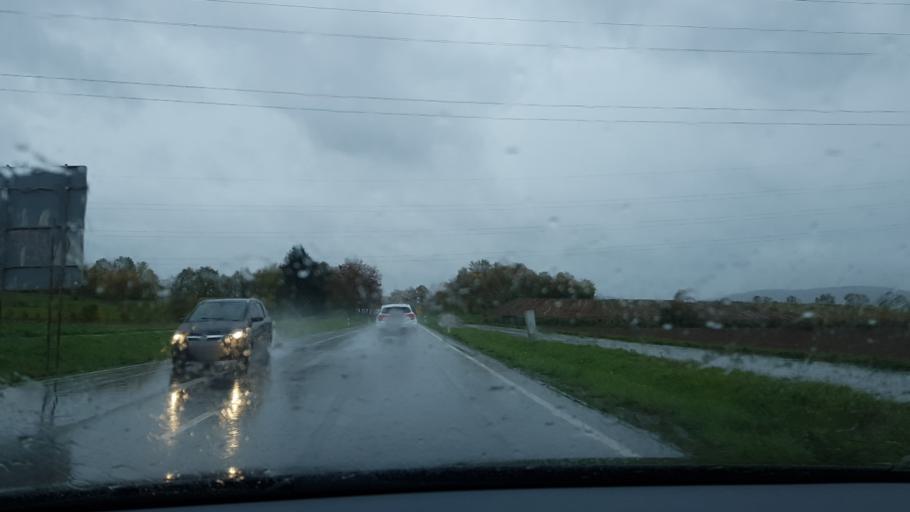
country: DE
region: Rheinland-Pfalz
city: Flussbach
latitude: 49.9940
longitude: 6.9210
